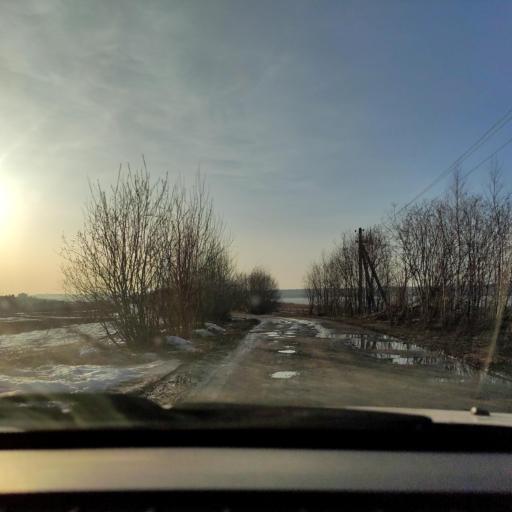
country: RU
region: Perm
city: Novyye Lyady
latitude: 58.1485
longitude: 56.5001
